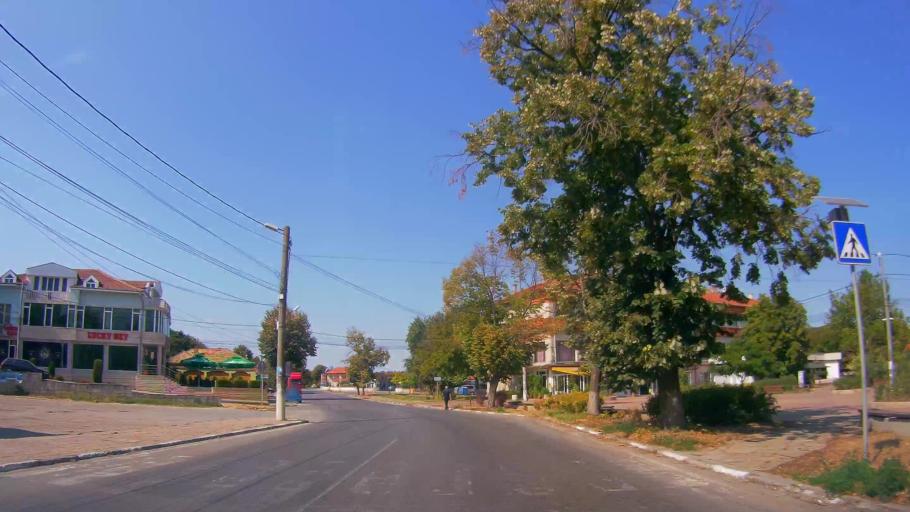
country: BG
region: Razgrad
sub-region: Obshtina Tsar Kaloyan
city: Tsar Kaloyan
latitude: 43.6084
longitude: 26.2375
